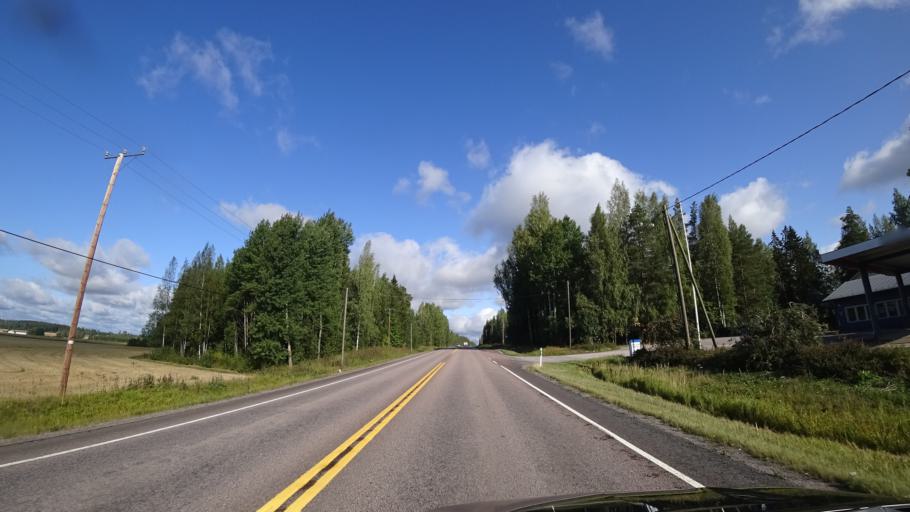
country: FI
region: Uusimaa
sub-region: Helsinki
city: Nurmijaervi
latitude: 60.5042
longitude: 24.9317
